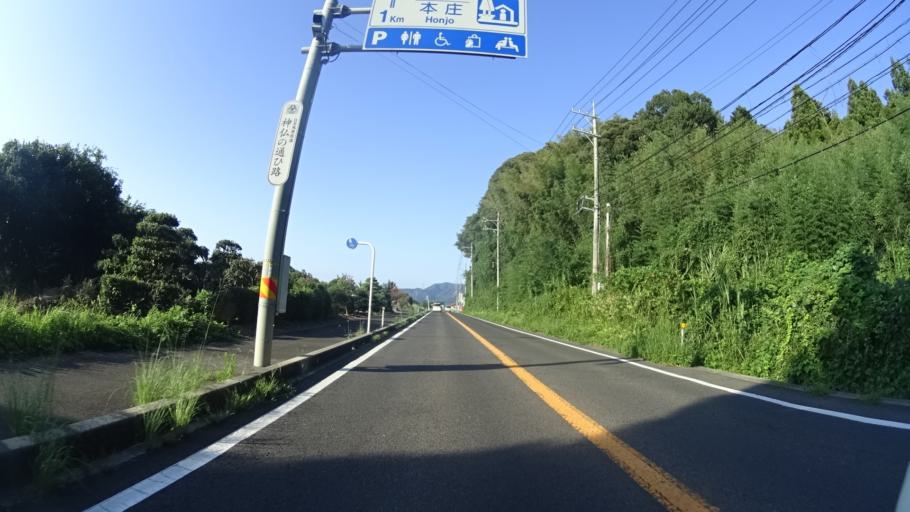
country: JP
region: Shimane
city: Sakaiminato
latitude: 35.5230
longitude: 133.1457
